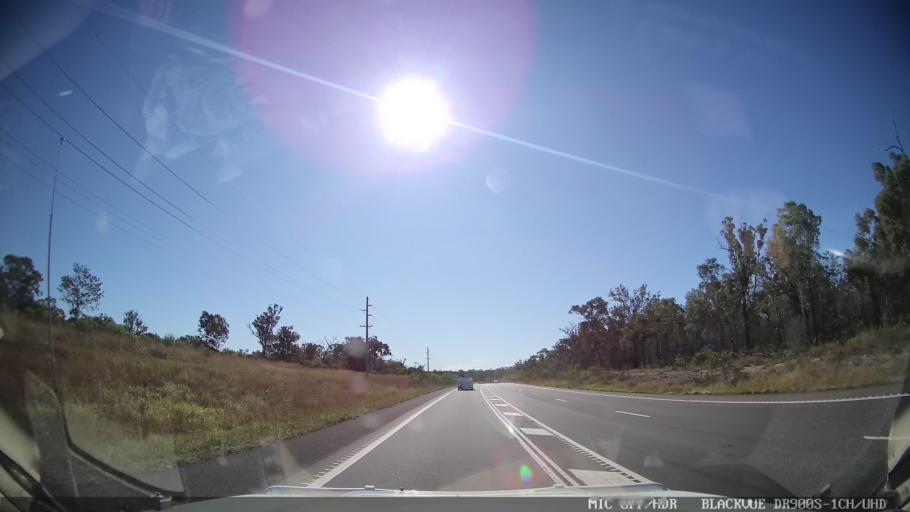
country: AU
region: Queensland
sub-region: Bundaberg
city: Childers
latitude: -25.2713
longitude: 152.3785
